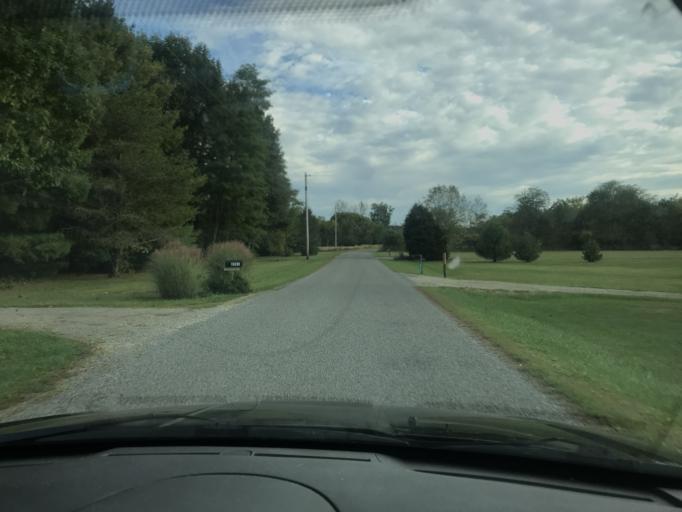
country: US
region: Ohio
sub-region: Logan County
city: West Liberty
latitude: 40.2560
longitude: -83.6974
